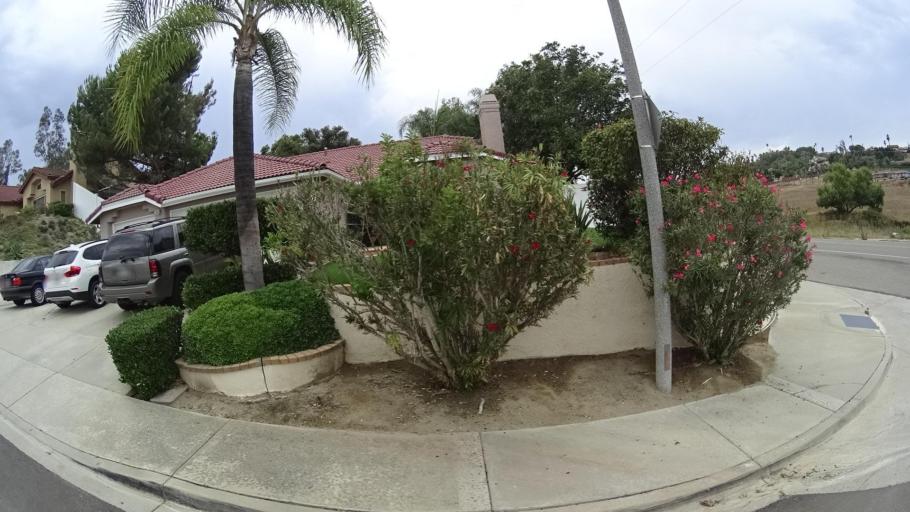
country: US
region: California
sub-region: San Diego County
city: Escondido
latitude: 33.1426
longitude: -117.1143
